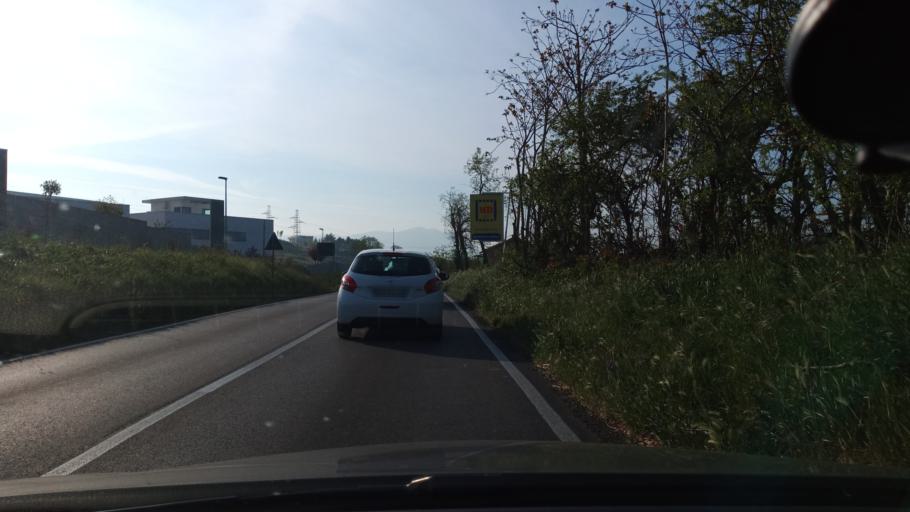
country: IT
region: Latium
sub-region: Citta metropolitana di Roma Capitale
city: Fiano Romano
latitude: 42.1679
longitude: 12.6392
